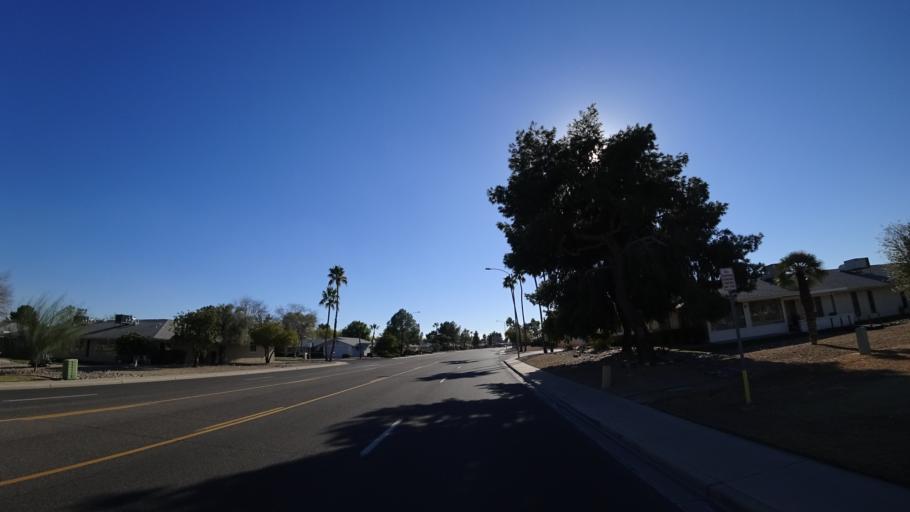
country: US
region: Arizona
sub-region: Maricopa County
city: Sun City West
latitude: 33.6552
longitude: -112.3324
